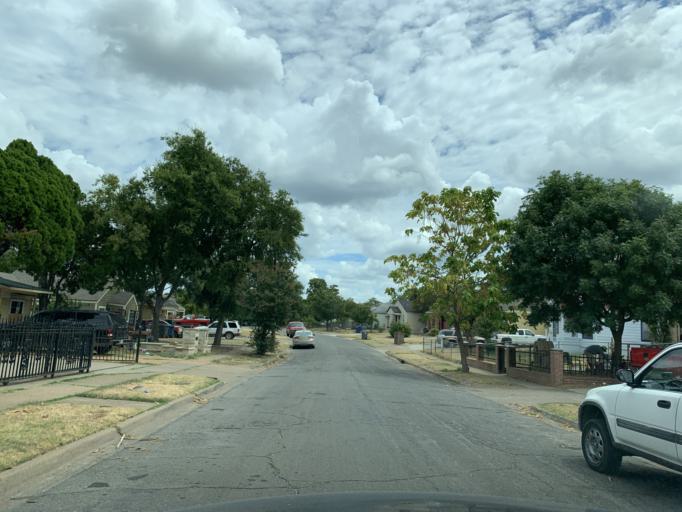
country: US
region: Texas
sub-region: Dallas County
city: Cockrell Hill
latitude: 32.7444
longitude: -96.8796
